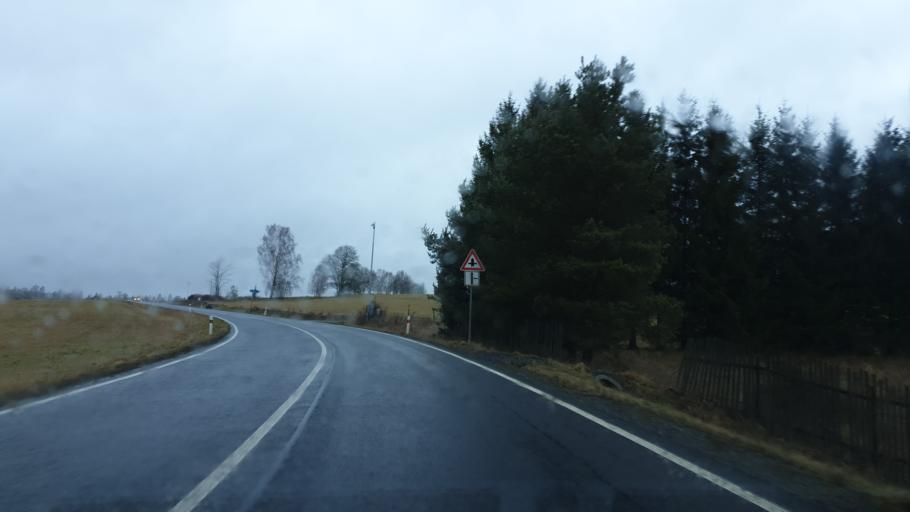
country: CZ
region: Karlovarsky
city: Hranice
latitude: 50.2910
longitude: 12.1814
